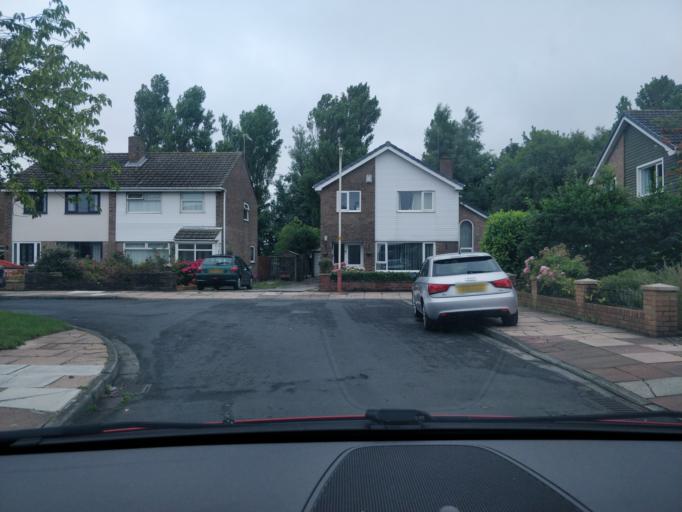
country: GB
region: England
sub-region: Lancashire
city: Banks
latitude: 53.6764
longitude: -2.9583
